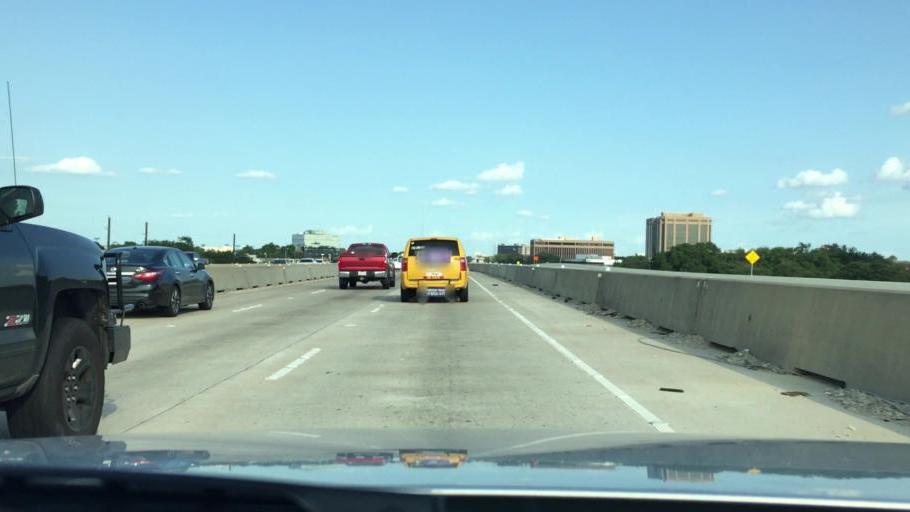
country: US
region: Texas
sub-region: Harris County
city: Hudson
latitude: 29.8503
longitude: -95.5078
